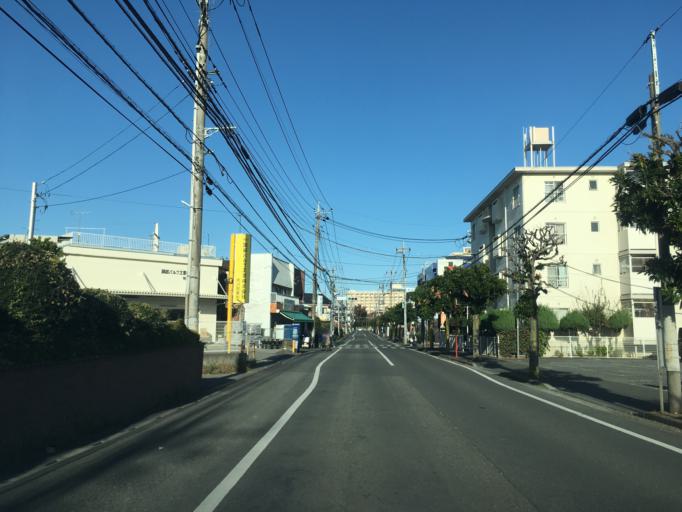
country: JP
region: Saitama
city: Tokorozawa
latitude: 35.7985
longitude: 139.4605
